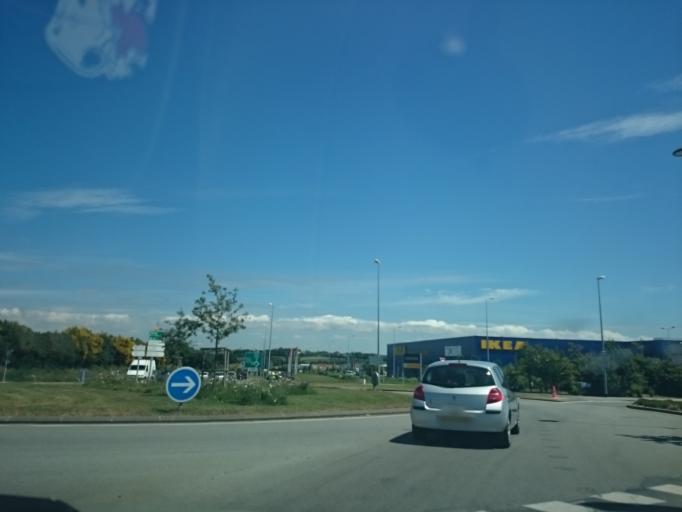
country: FR
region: Brittany
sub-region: Departement du Finistere
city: Gouesnou
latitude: 48.4192
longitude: -4.4437
